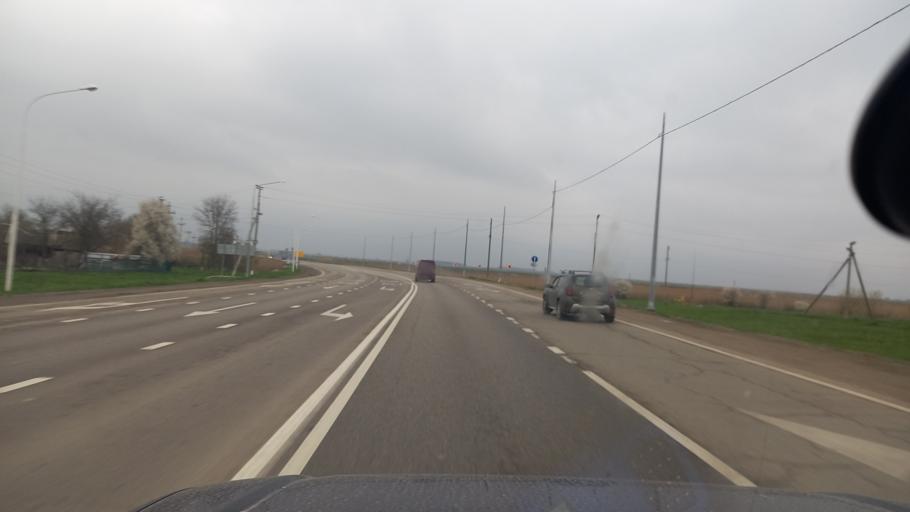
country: RU
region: Krasnodarskiy
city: Novomyshastovskaya
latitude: 45.1828
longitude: 38.5633
